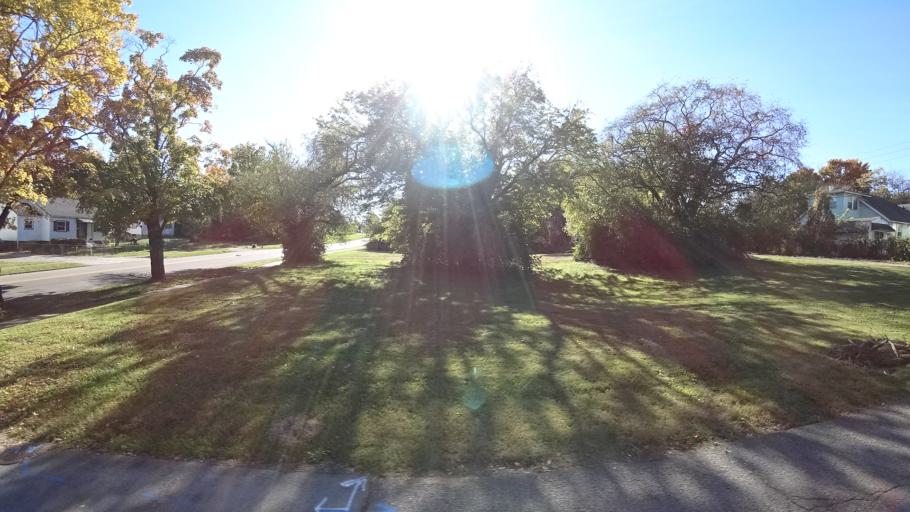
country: US
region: Tennessee
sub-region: Knox County
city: Knoxville
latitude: 35.9848
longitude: -83.8918
